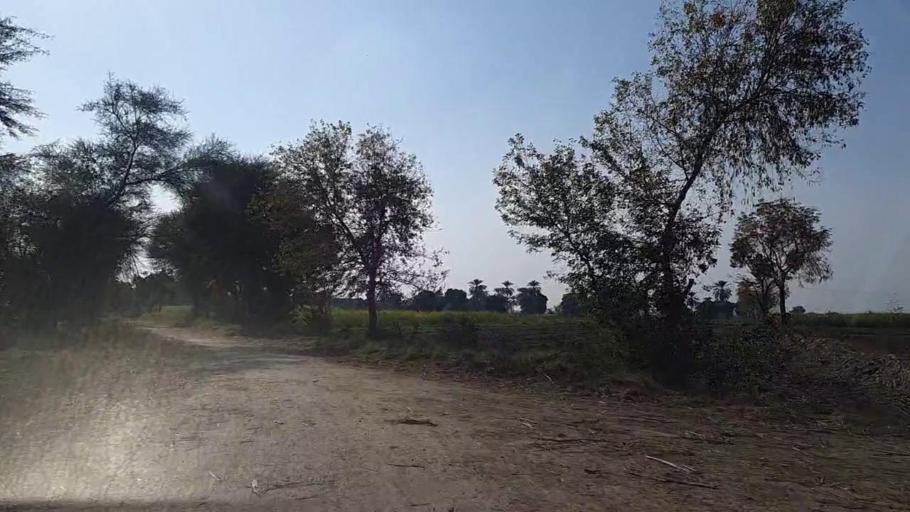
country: PK
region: Sindh
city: Daur
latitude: 26.3851
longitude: 68.3256
